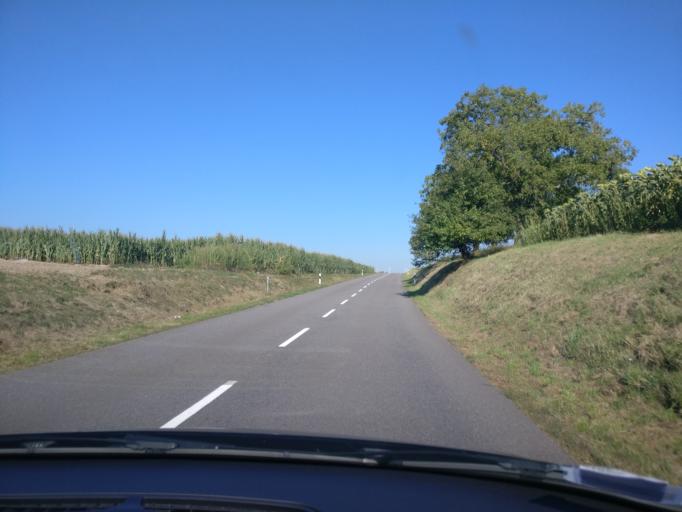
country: LU
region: Grevenmacher
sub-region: Canton de Grevenmacher
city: Betzdorf
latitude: 49.7203
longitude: 6.3162
